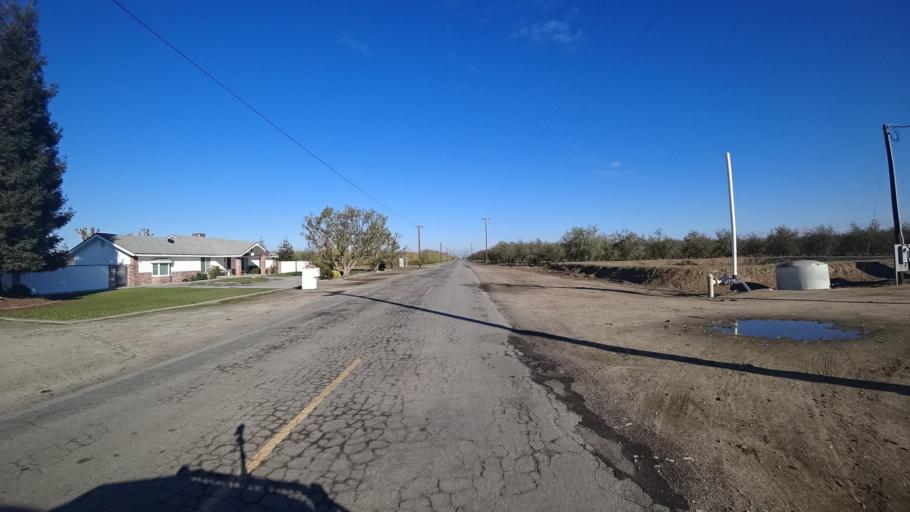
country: US
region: California
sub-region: Kern County
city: Delano
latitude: 35.7249
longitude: -119.3119
